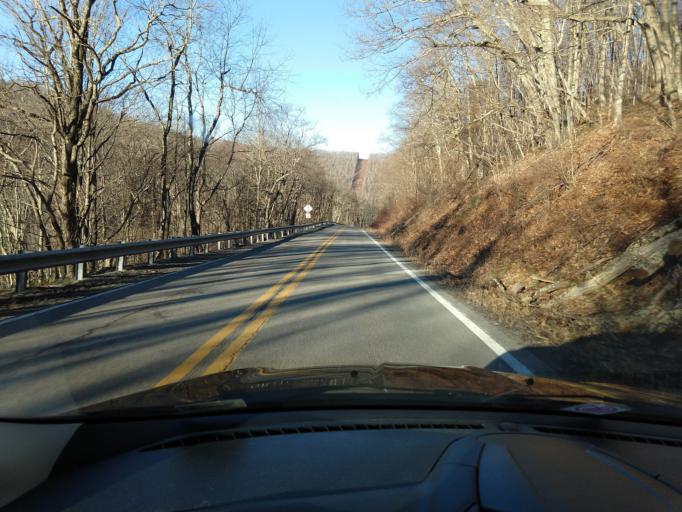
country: US
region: Virginia
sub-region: Highland County
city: Monterey
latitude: 38.4941
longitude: -79.7042
